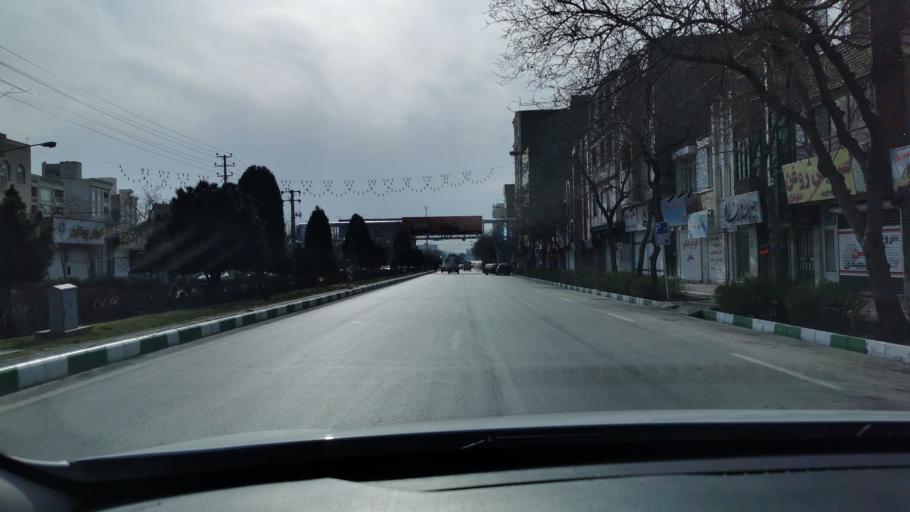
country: IR
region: Razavi Khorasan
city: Mashhad
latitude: 36.2975
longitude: 59.5268
